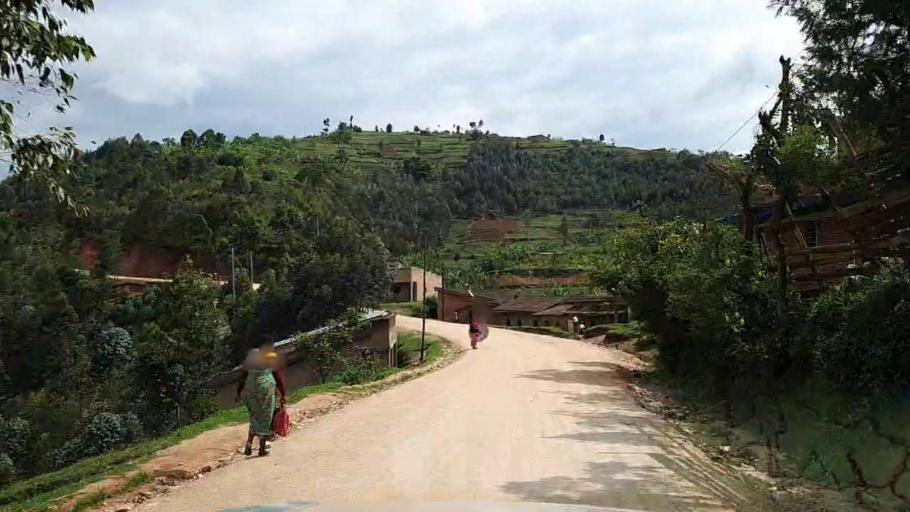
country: RW
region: Southern Province
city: Nzega
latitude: -2.3368
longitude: 29.4445
